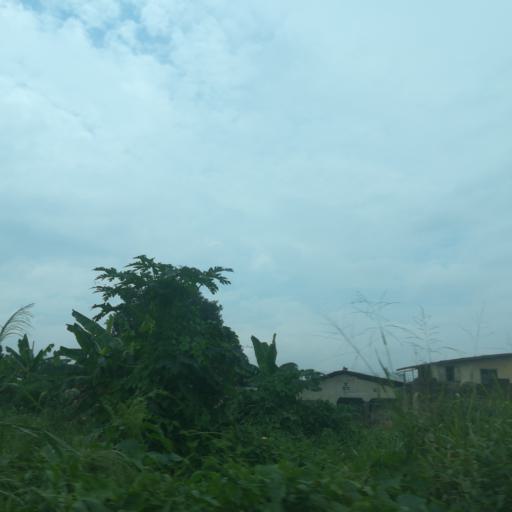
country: NG
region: Lagos
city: Ejirin
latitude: 6.6466
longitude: 3.7706
